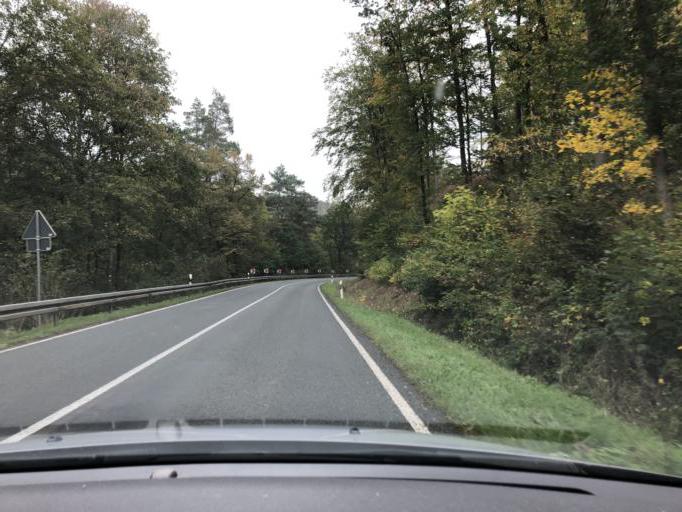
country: DE
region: Thuringia
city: Auleben
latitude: 51.3860
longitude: 10.9119
